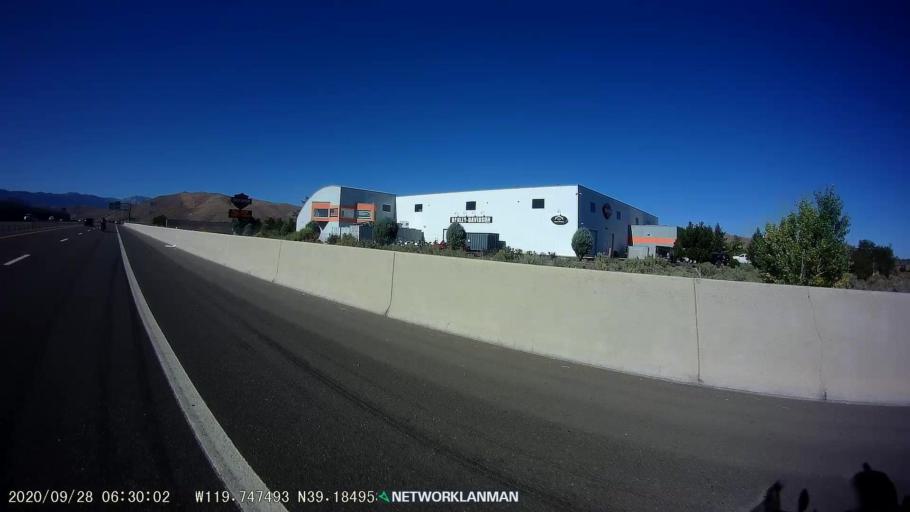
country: US
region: Nevada
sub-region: Carson City
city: Carson City
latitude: 39.1851
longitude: -119.7479
